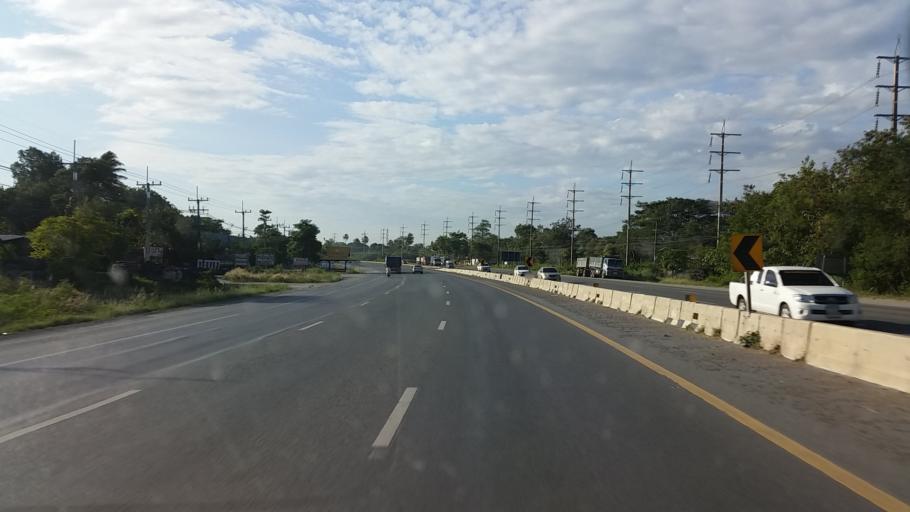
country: TH
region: Sara Buri
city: Chaloem Phra Kiat
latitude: 14.6548
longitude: 100.8846
